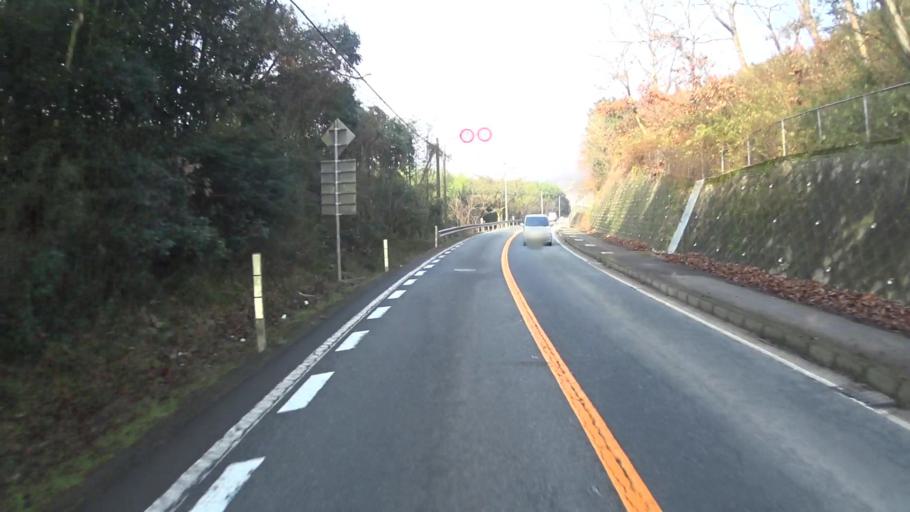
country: JP
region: Kyoto
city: Ayabe
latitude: 35.2875
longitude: 135.2873
